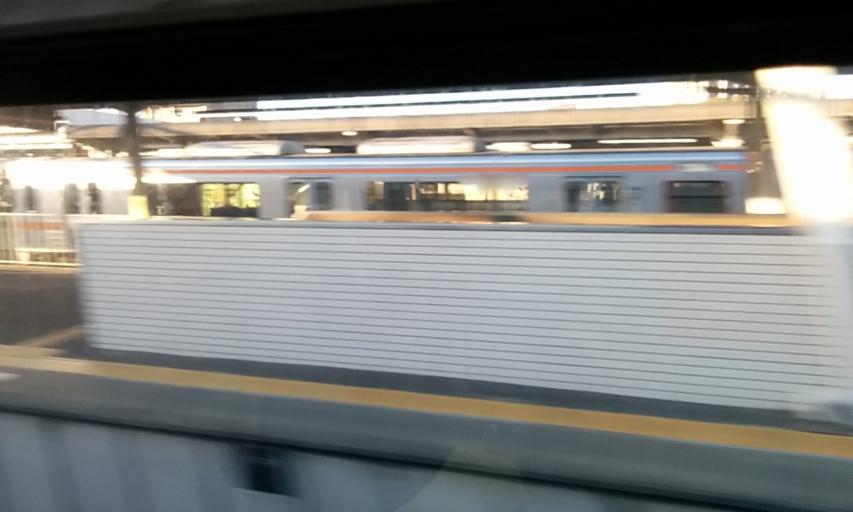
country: JP
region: Aichi
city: Seto
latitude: 35.2644
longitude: 137.0433
